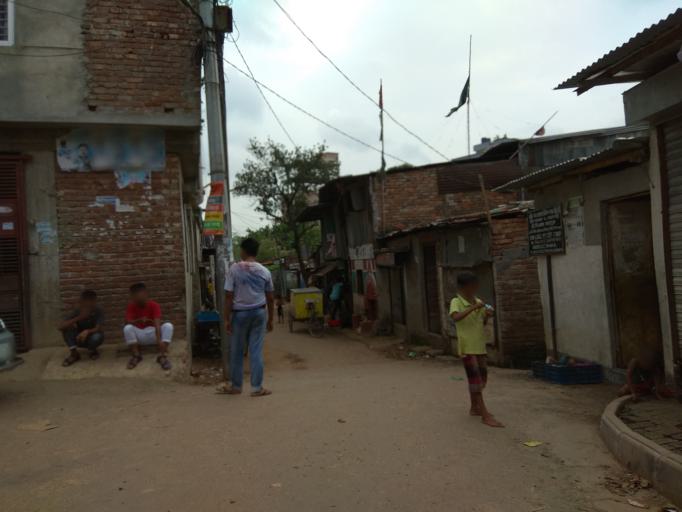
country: BD
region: Dhaka
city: Tungi
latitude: 23.8140
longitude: 90.3765
